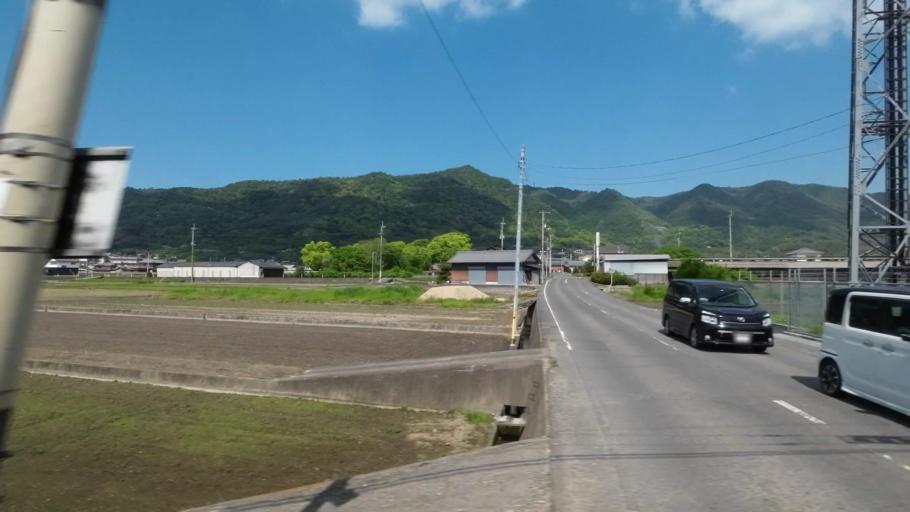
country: JP
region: Kagawa
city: Kan'onjicho
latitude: 34.1570
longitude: 133.6884
